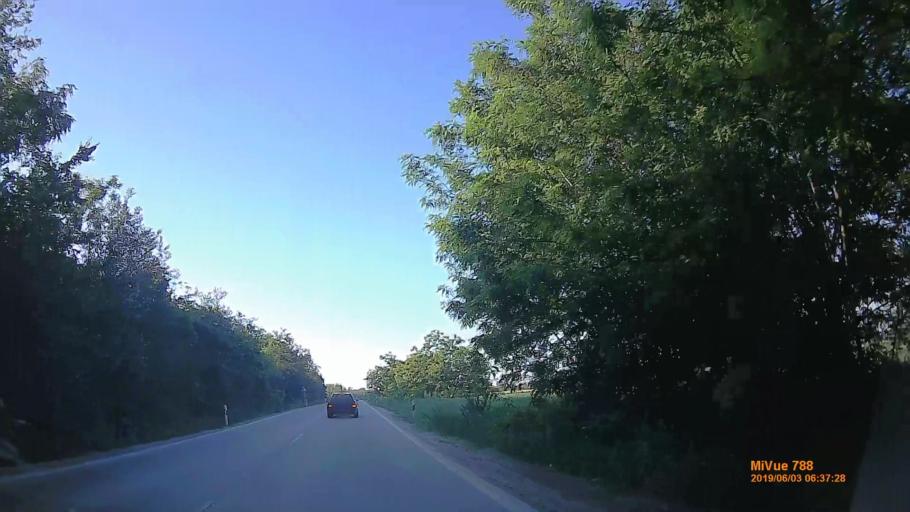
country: HU
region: Pest
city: Dunavarsany
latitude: 47.3001
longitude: 19.0885
